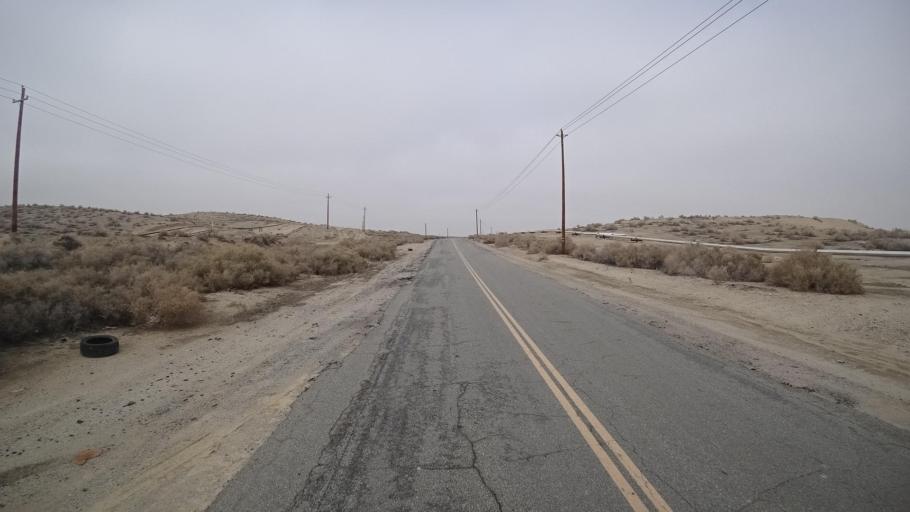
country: US
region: California
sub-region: Kern County
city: Maricopa
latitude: 35.0876
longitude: -119.3997
